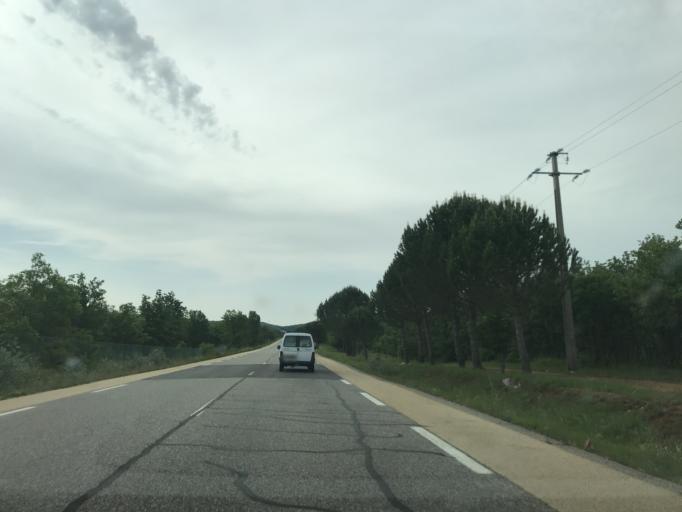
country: FR
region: Provence-Alpes-Cote d'Azur
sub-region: Departement du Var
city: Rians
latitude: 43.5601
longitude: 5.7873
